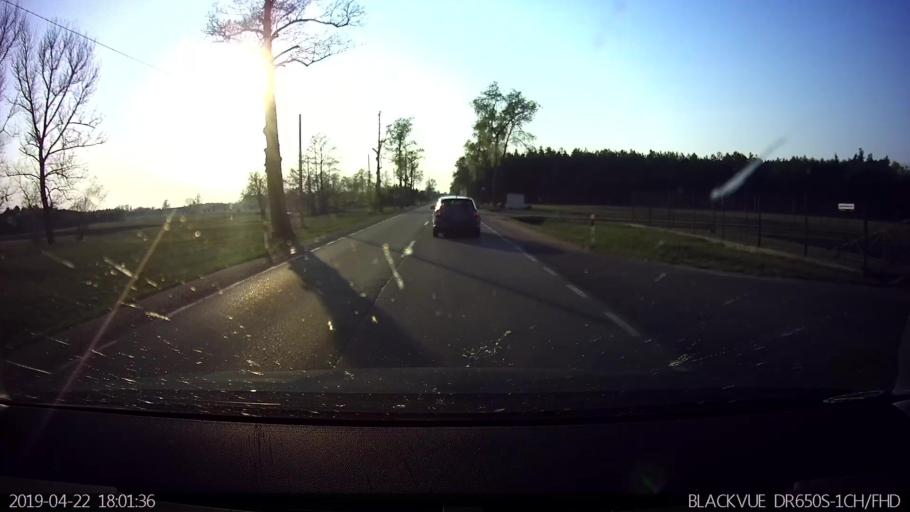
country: PL
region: Masovian Voivodeship
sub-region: Powiat wegrowski
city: Korytnica
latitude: 52.4803
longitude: 21.8260
